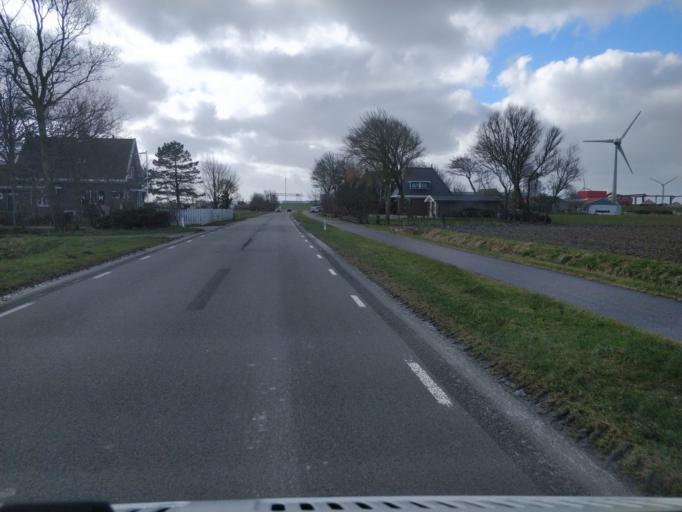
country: NL
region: Friesland
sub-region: Gemeente Harlingen
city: Harlingen
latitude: 53.1978
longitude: 5.4460
